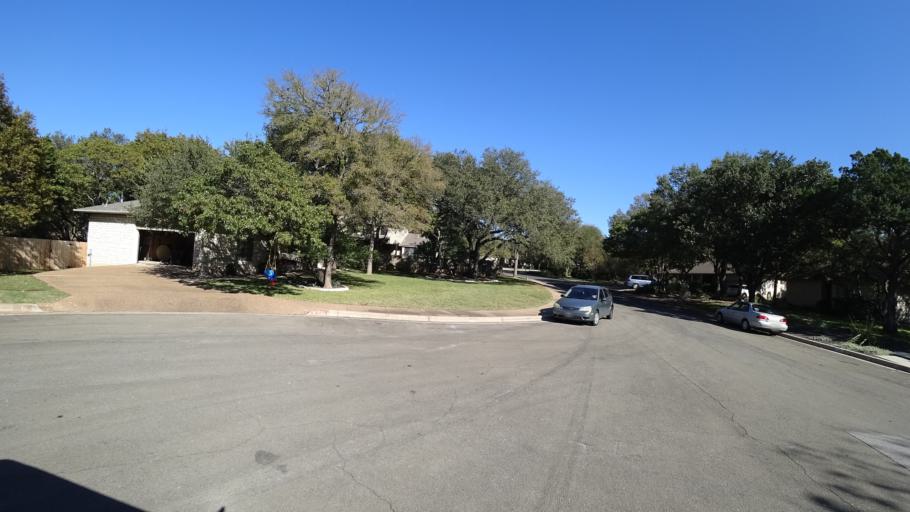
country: US
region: Texas
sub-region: Williamson County
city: Jollyville
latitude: 30.4180
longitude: -97.7726
